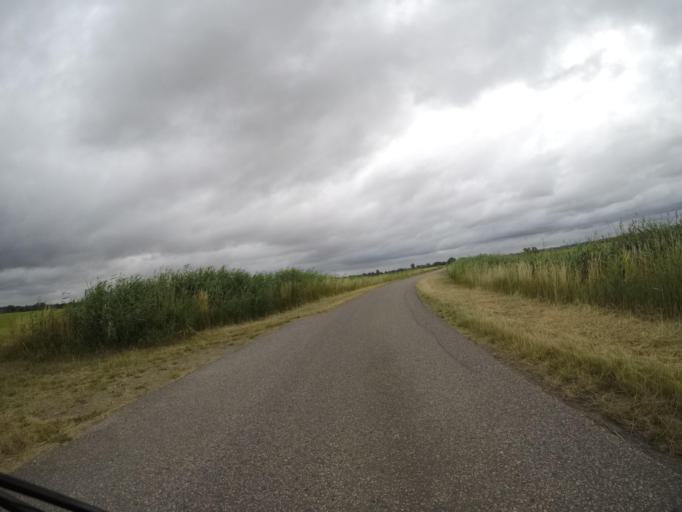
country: DE
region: Lower Saxony
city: Hitzacker
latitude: 53.1665
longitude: 11.0833
